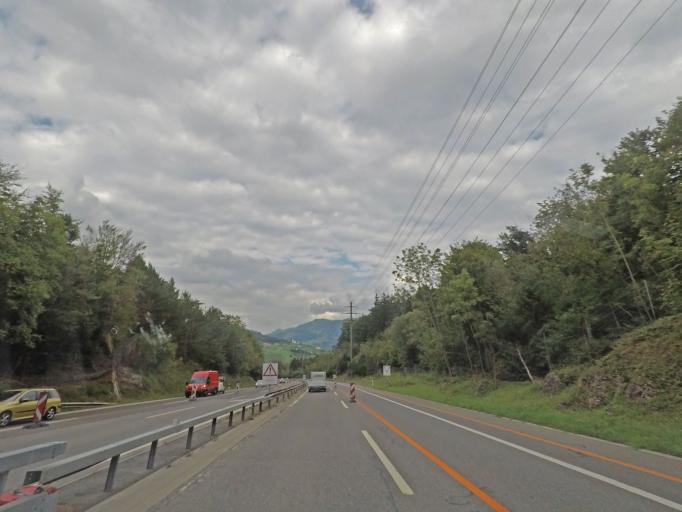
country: CH
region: Schwyz
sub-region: Bezirk Schwyz
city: Goldau
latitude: 47.0449
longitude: 8.5570
